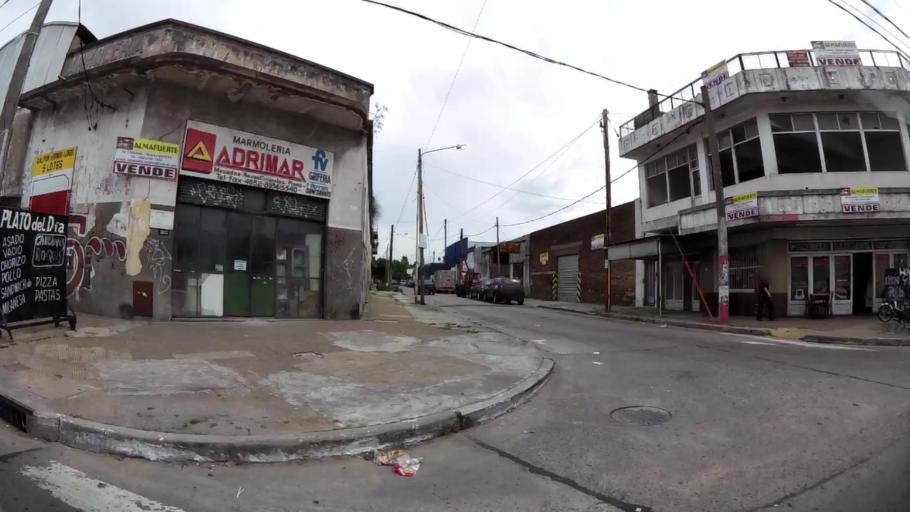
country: AR
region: Buenos Aires
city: San Justo
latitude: -34.6898
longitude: -58.5256
